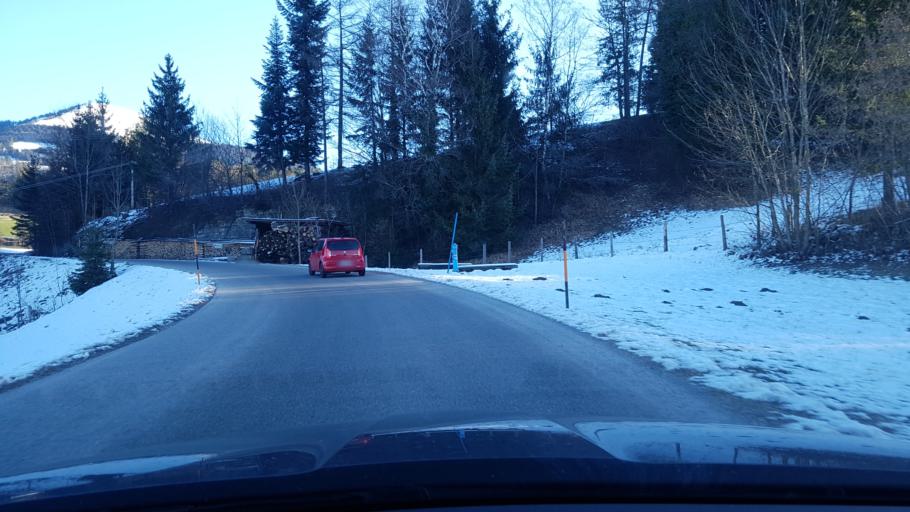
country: AT
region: Salzburg
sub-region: Politischer Bezirk Hallein
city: Kuchl
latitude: 47.6587
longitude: 13.1817
